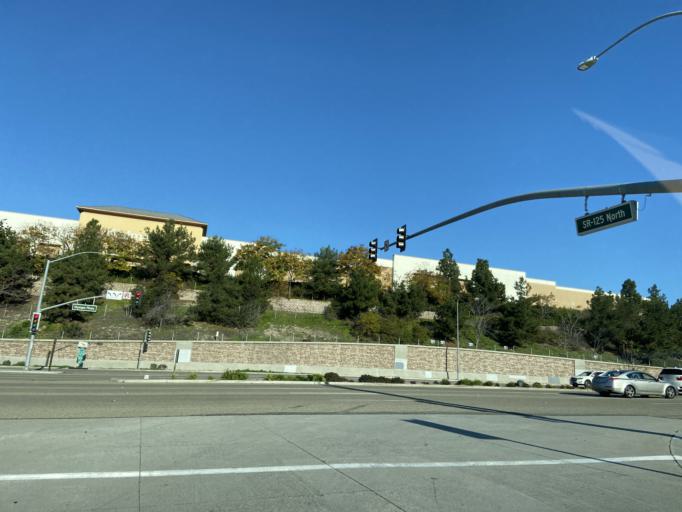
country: US
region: California
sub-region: San Diego County
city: Bonita
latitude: 32.6303
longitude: -116.9695
